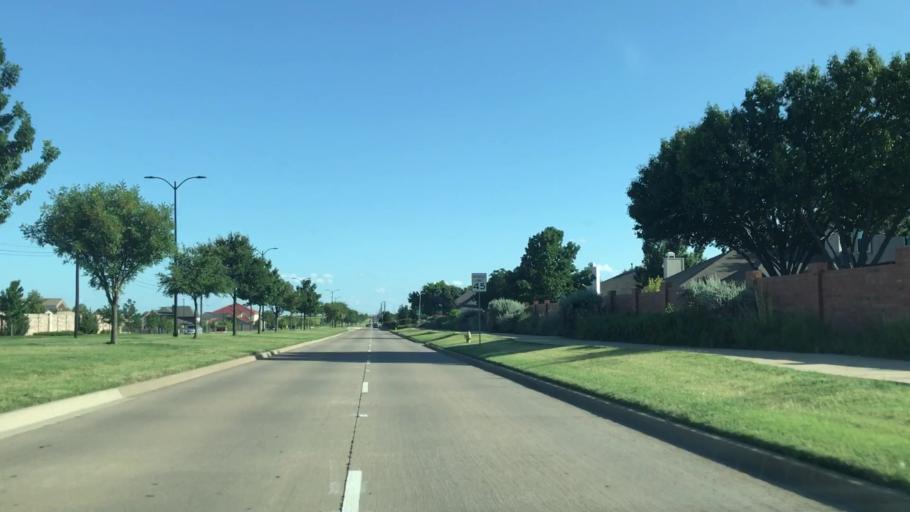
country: US
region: Texas
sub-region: Collin County
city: Frisco
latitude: 33.1284
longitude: -96.7681
